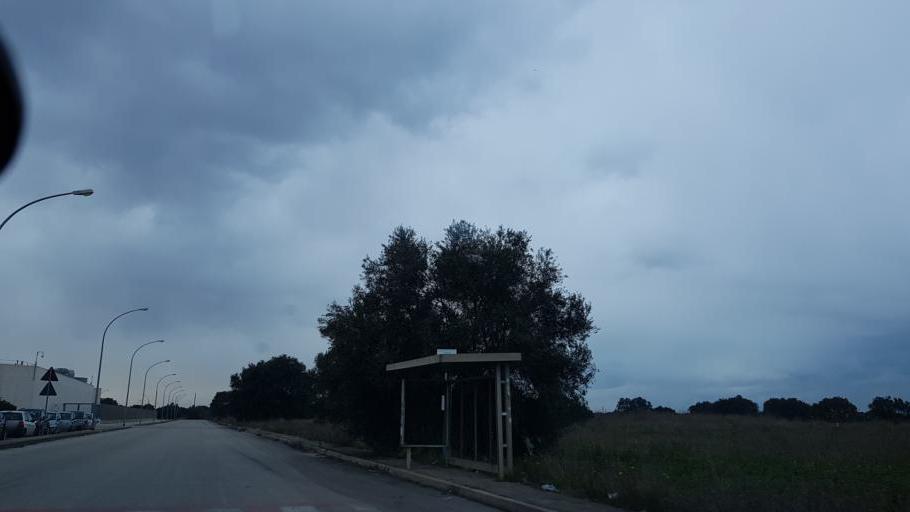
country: IT
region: Apulia
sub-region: Provincia di Brindisi
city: Mesagne
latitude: 40.5798
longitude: 17.8391
